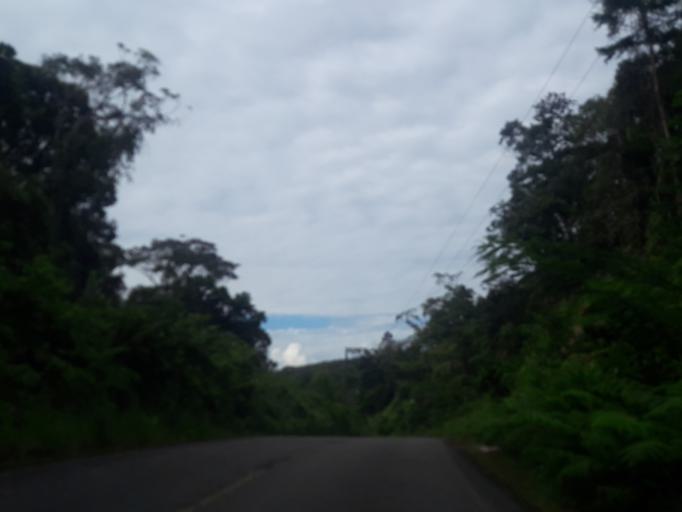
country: EC
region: Napo
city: Tena
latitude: -1.0433
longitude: -77.8982
